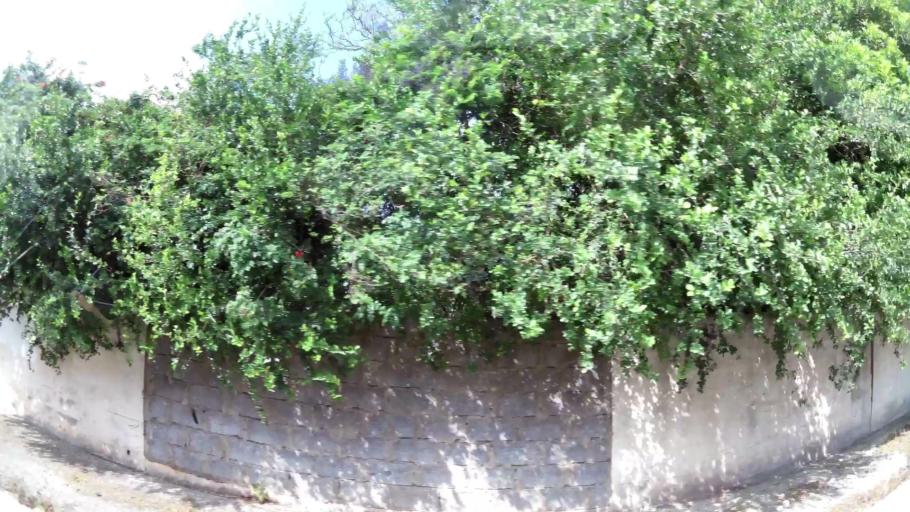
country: MA
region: Rabat-Sale-Zemmour-Zaer
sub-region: Rabat
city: Rabat
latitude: 33.9719
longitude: -6.8524
